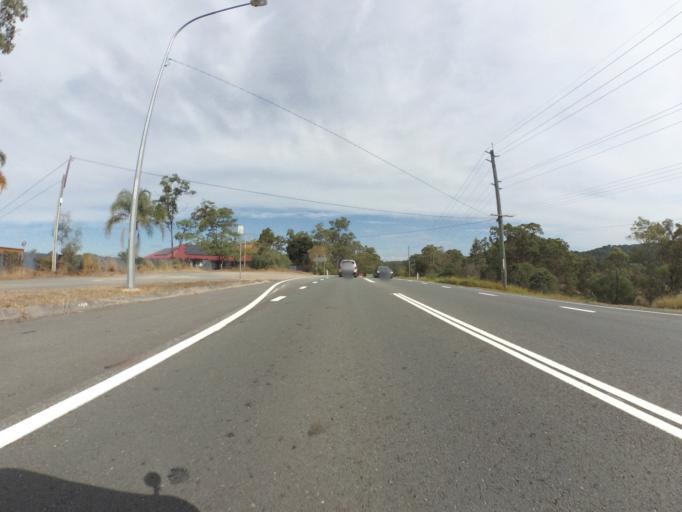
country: AU
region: Queensland
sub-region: Brisbane
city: Pullenvale
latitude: -27.5410
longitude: 152.8942
